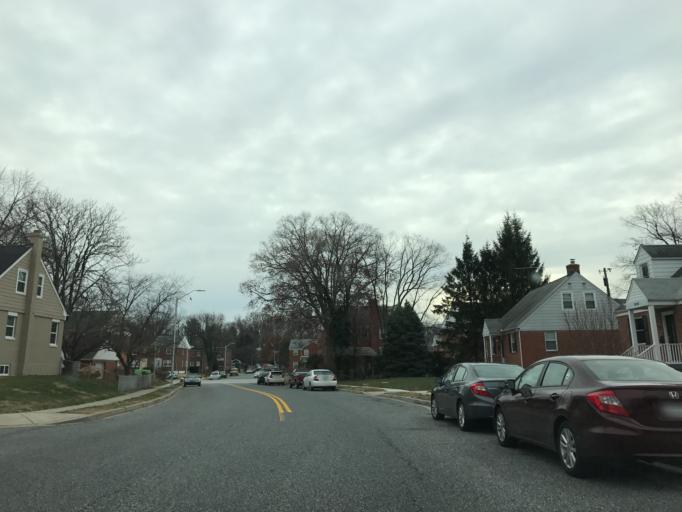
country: US
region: Maryland
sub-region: Baltimore County
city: Parkville
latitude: 39.3511
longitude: -76.5465
